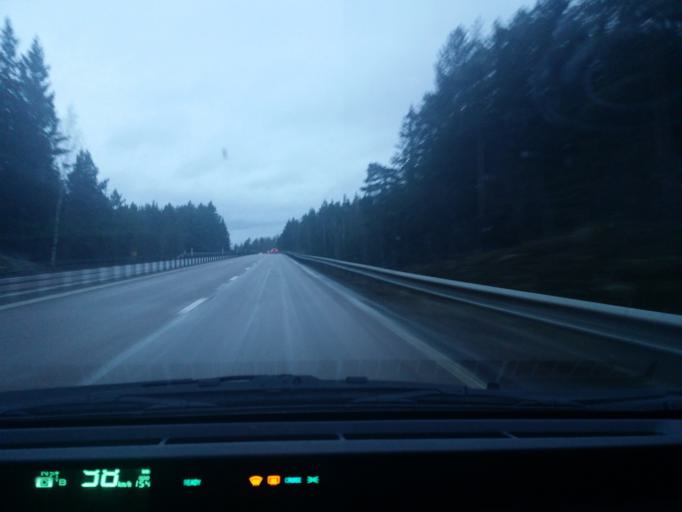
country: SE
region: Soedermanland
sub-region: Eskilstuna Kommun
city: Kvicksund
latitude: 59.4191
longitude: 16.3656
